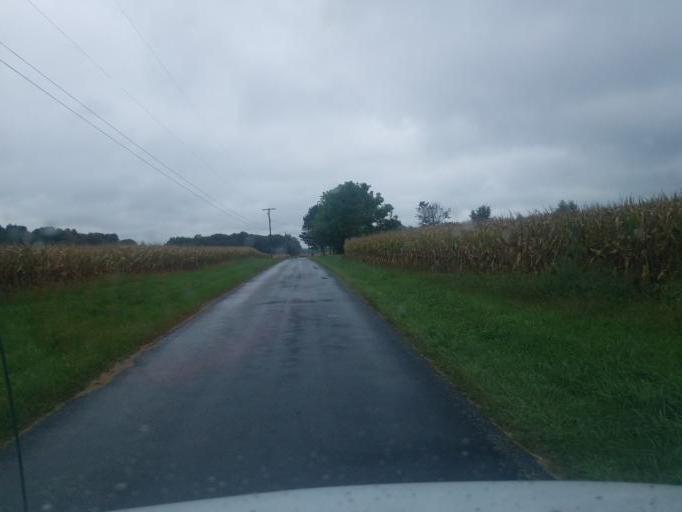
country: US
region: Ohio
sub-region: Ashland County
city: Ashland
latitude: 40.8426
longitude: -82.1780
